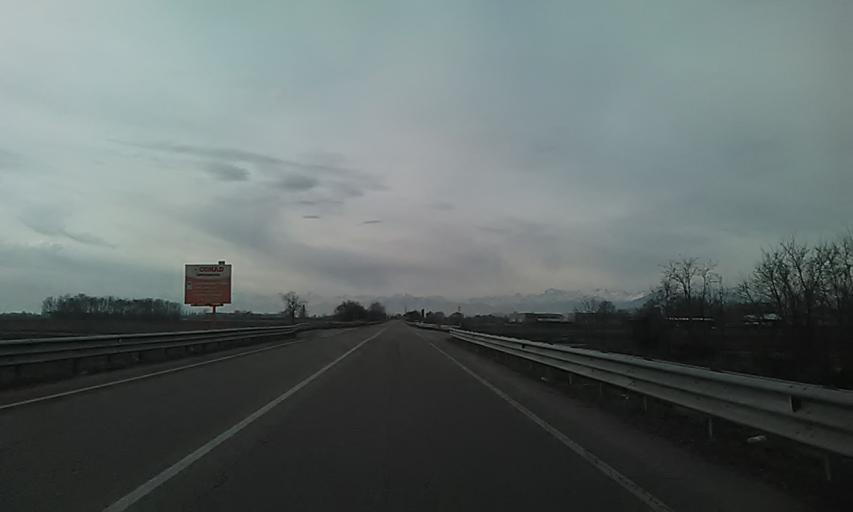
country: IT
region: Piedmont
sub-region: Provincia di Vercelli
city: Cigliano
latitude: 45.2965
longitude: 8.0305
